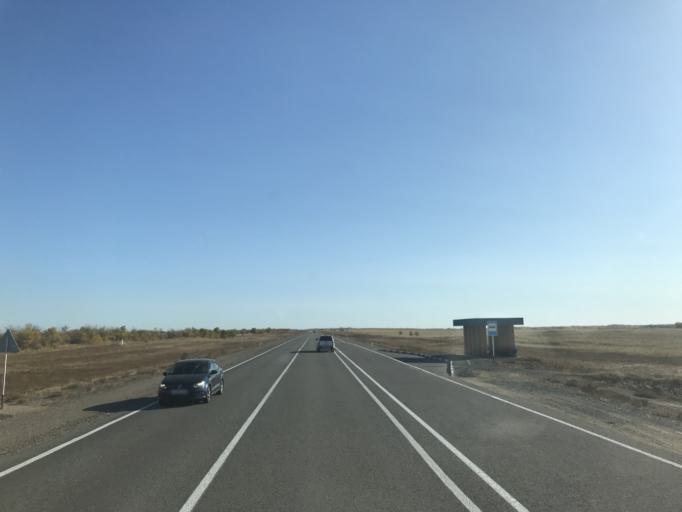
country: KZ
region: Pavlodar
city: Koktobe
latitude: 51.8124
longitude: 77.4725
